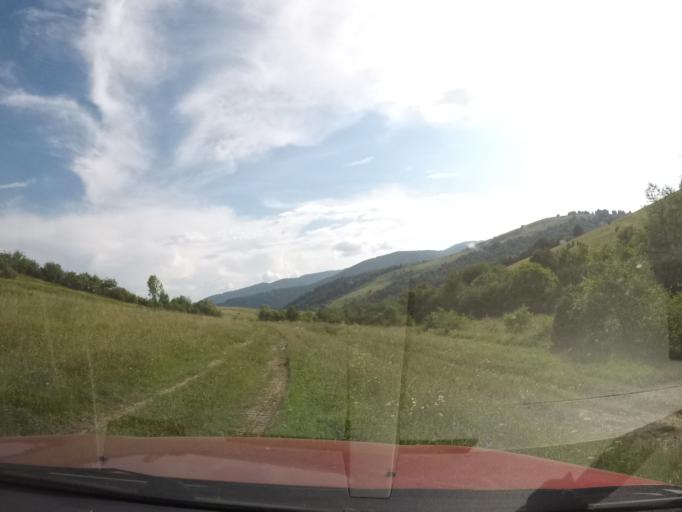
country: UA
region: Zakarpattia
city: Velykyi Bereznyi
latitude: 49.0295
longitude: 22.6379
